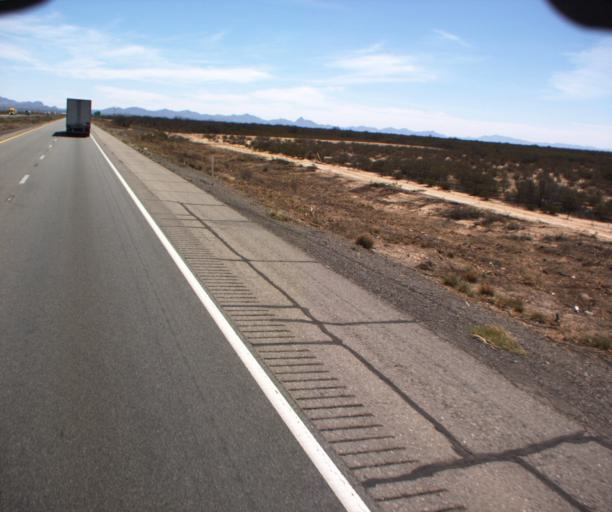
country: US
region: Arizona
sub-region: Cochise County
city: Willcox
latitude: 32.2804
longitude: -109.2810
